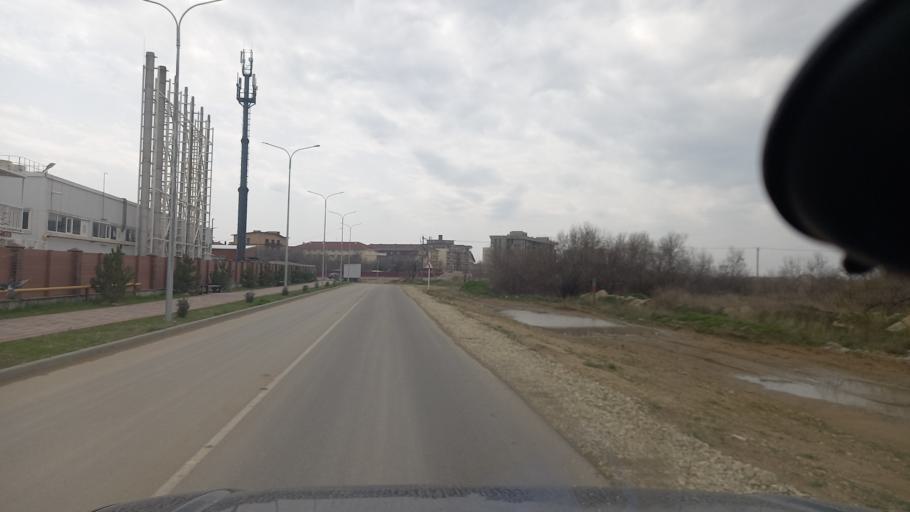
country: RU
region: Krasnodarskiy
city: Vityazevo
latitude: 44.9941
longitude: 37.2444
